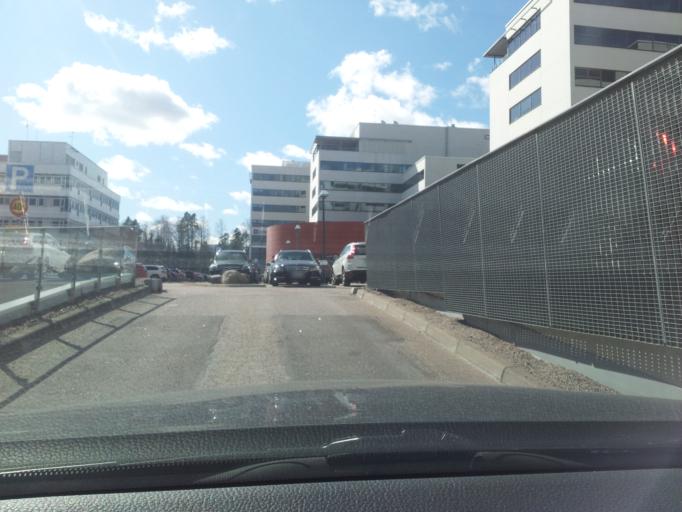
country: FI
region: Uusimaa
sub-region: Helsinki
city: Otaniemi
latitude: 60.1782
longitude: 24.8342
